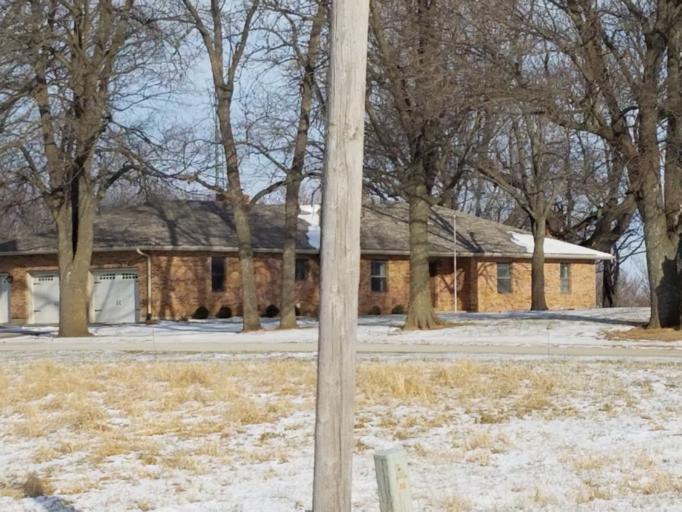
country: US
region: Missouri
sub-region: Carroll County
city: Carrollton
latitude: 39.2039
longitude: -93.4467
